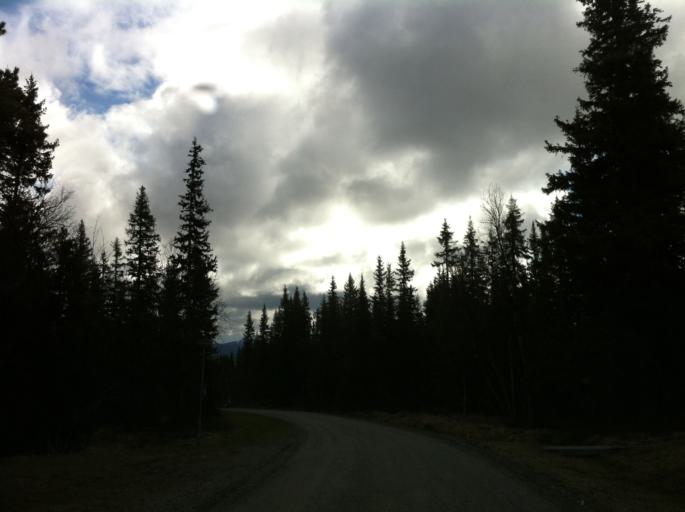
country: NO
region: Hedmark
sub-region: Engerdal
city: Engerdal
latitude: 62.5408
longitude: 12.4458
